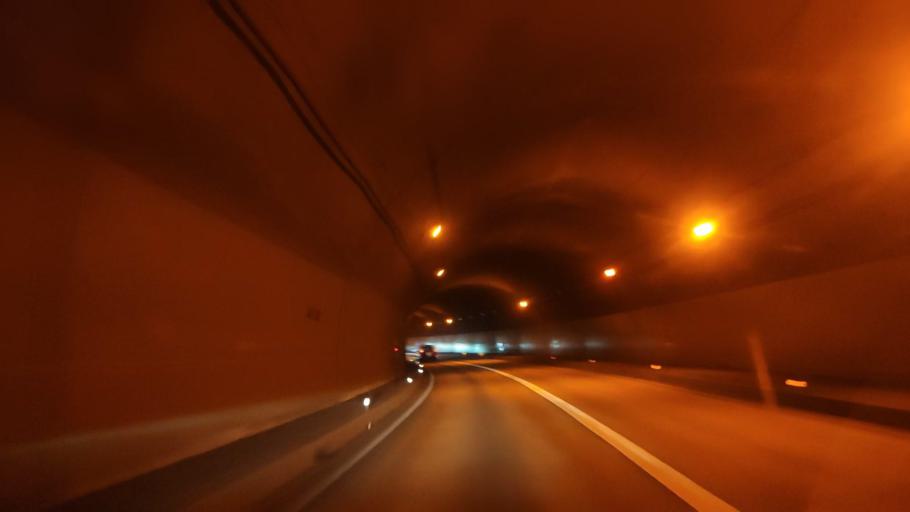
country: JP
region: Nagano
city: Okaya
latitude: 36.0893
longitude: 138.0607
